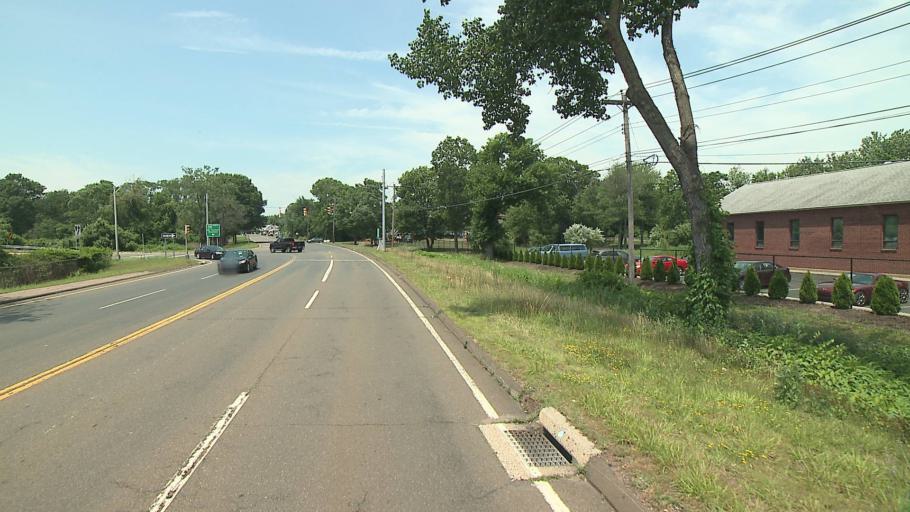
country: US
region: Connecticut
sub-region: New Haven County
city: Hamden
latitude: 41.3798
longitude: -72.8800
